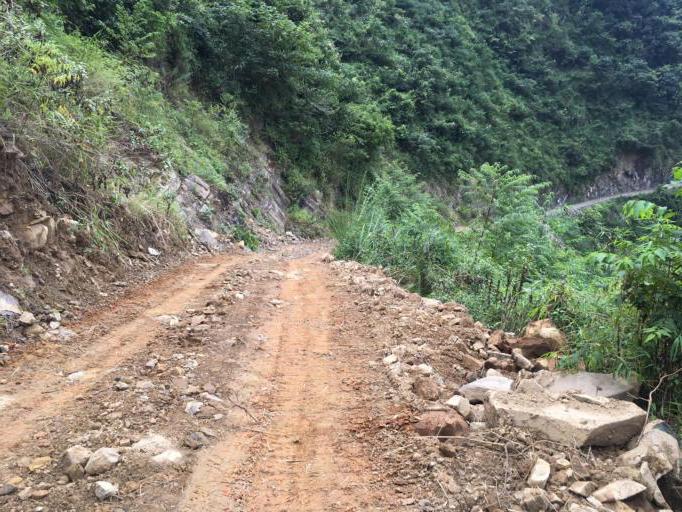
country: CN
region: Guangxi Zhuangzu Zizhiqu
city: Tongle
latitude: 25.3014
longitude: 106.1432
